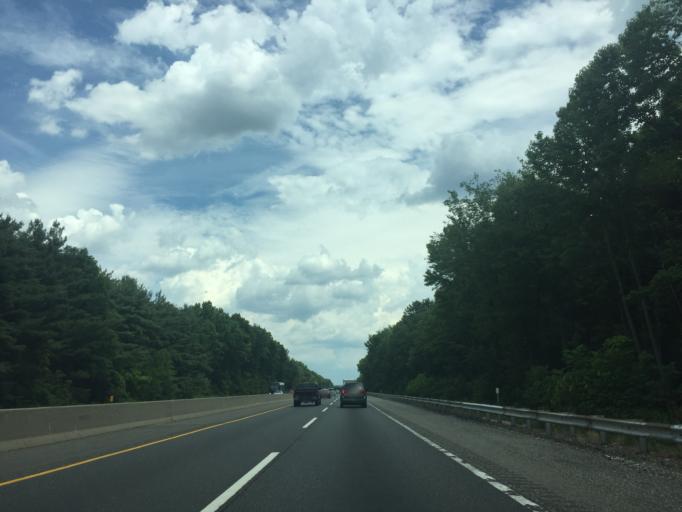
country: US
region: New Jersey
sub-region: Camden County
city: Runnemede
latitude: 39.8615
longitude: -75.0647
